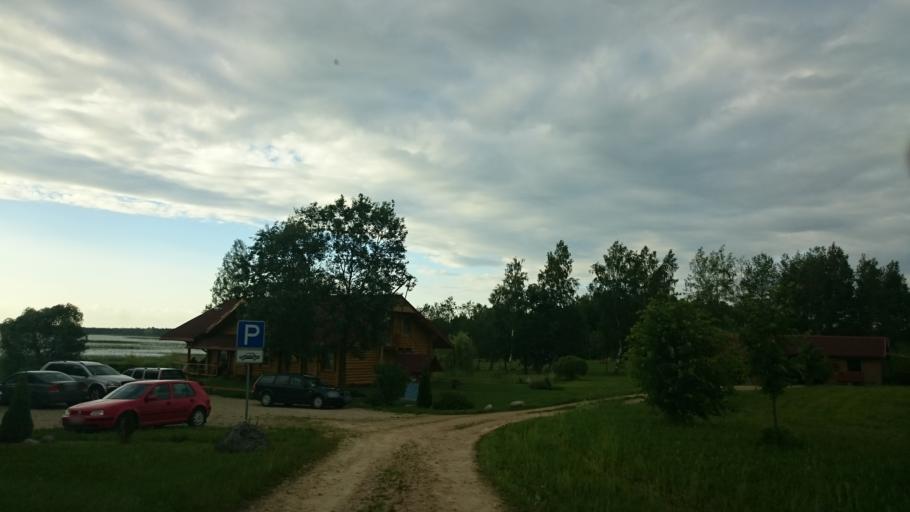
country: LV
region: Ludzas Rajons
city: Ludza
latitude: 56.5519
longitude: 27.6459
